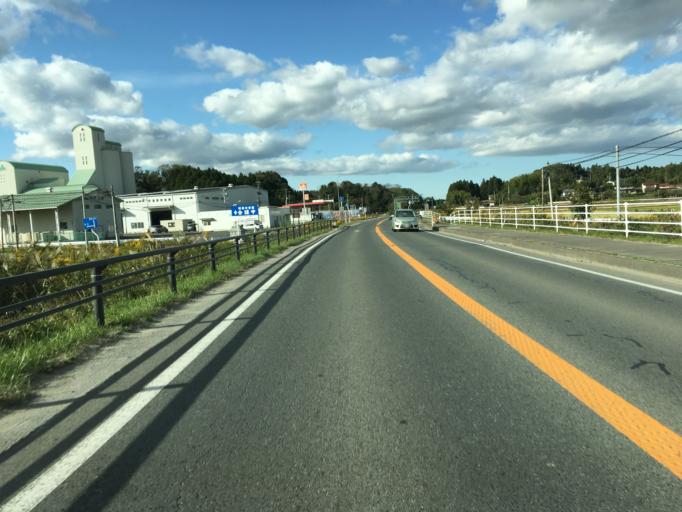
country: JP
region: Miyagi
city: Marumori
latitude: 37.8800
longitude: 140.9153
